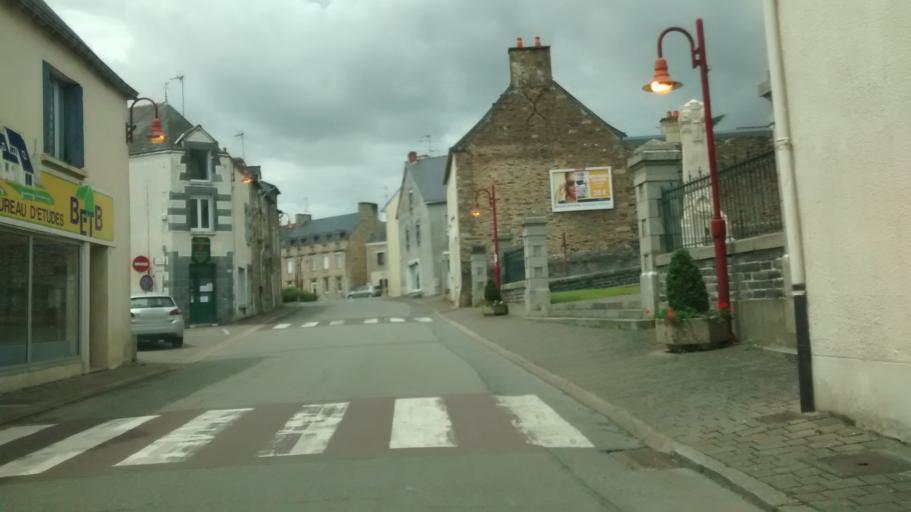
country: FR
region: Brittany
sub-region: Departement du Morbihan
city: Carentoir
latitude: 47.8168
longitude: -2.1335
